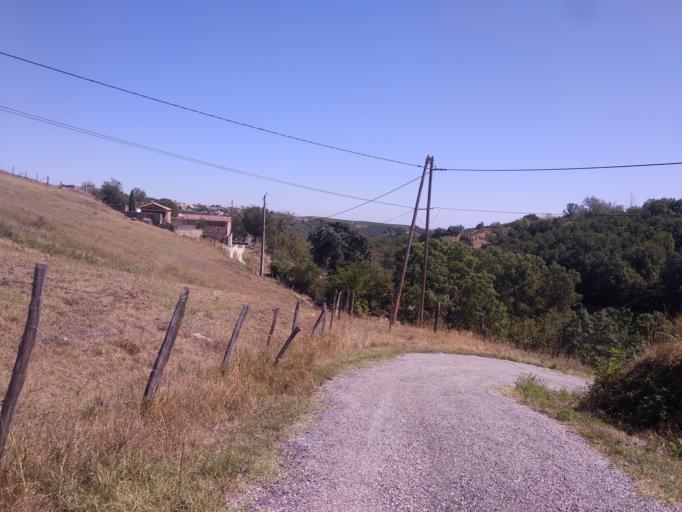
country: FR
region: Rhone-Alpes
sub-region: Departement de l'Ardeche
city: Sarras
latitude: 45.1835
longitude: 4.7568
